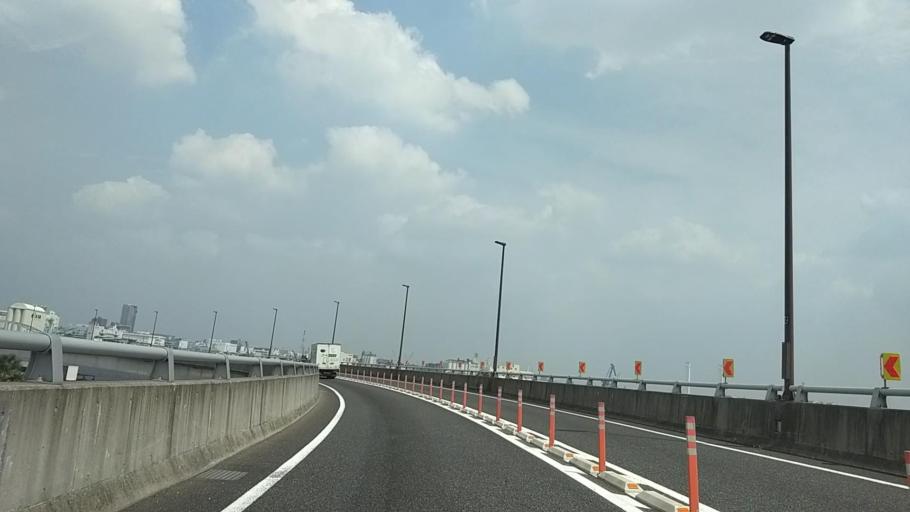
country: JP
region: Kanagawa
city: Yokohama
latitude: 35.4671
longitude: 139.6400
